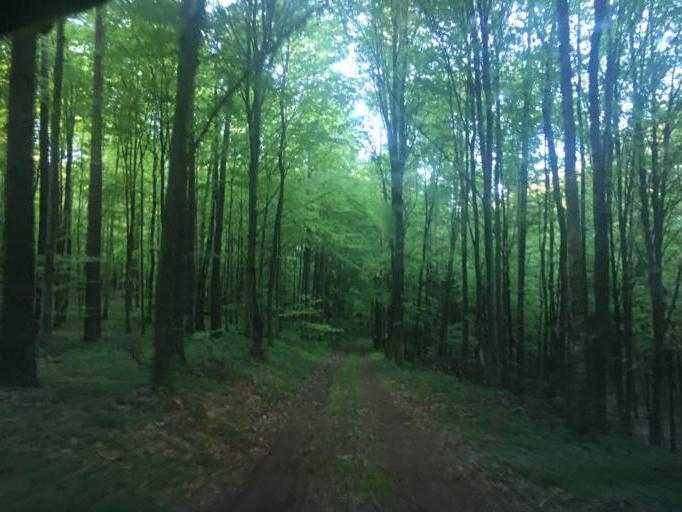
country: PL
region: Kujawsko-Pomorskie
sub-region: Powiat brodnicki
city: Gorzno
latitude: 53.2212
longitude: 19.7235
